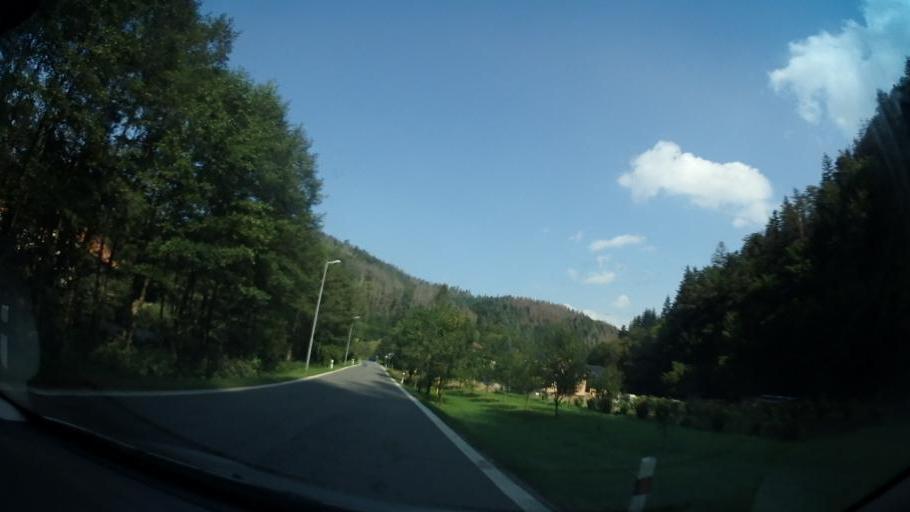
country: CZ
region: South Moravian
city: Olesnice
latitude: 49.5321
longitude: 16.3534
